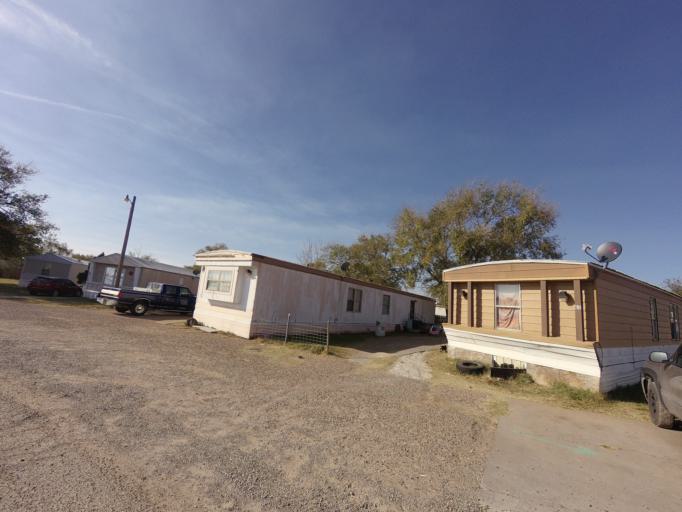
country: US
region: New Mexico
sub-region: Curry County
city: Clovis
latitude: 34.4109
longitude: -103.1748
